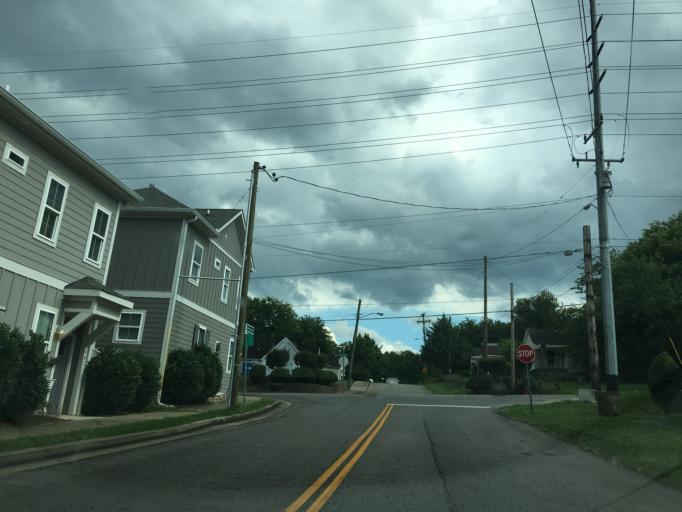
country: US
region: Tennessee
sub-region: Davidson County
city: Nashville
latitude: 36.1630
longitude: -86.8084
